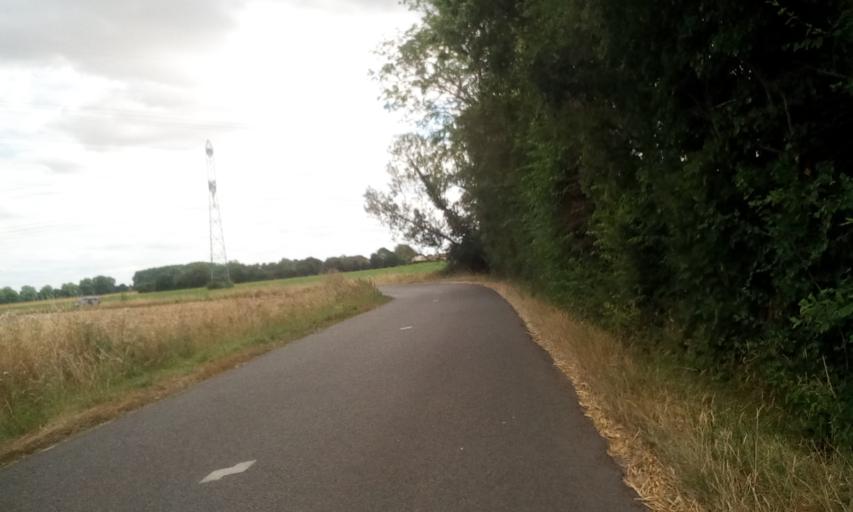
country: FR
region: Lower Normandy
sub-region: Departement du Calvados
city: Bellengreville
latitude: 49.1351
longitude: -0.2045
